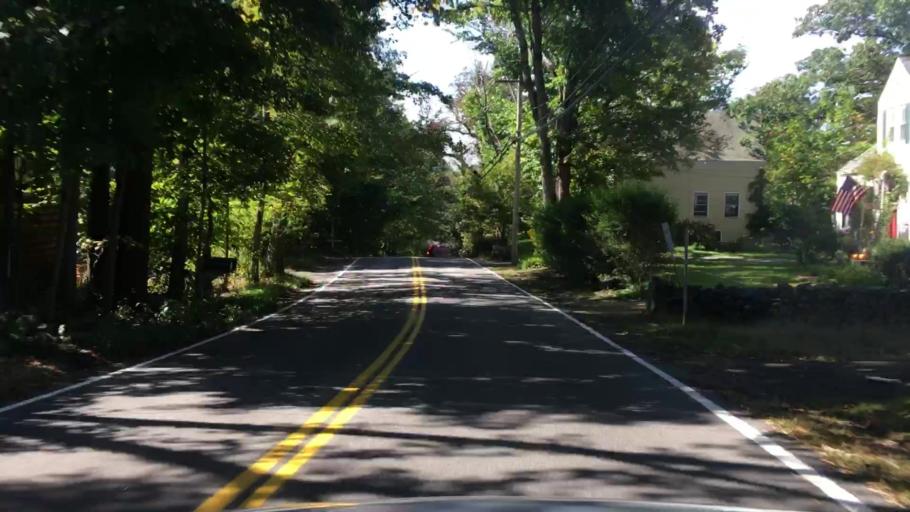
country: US
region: Maine
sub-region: York County
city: Kittery Point
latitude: 43.0863
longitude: -70.6901
